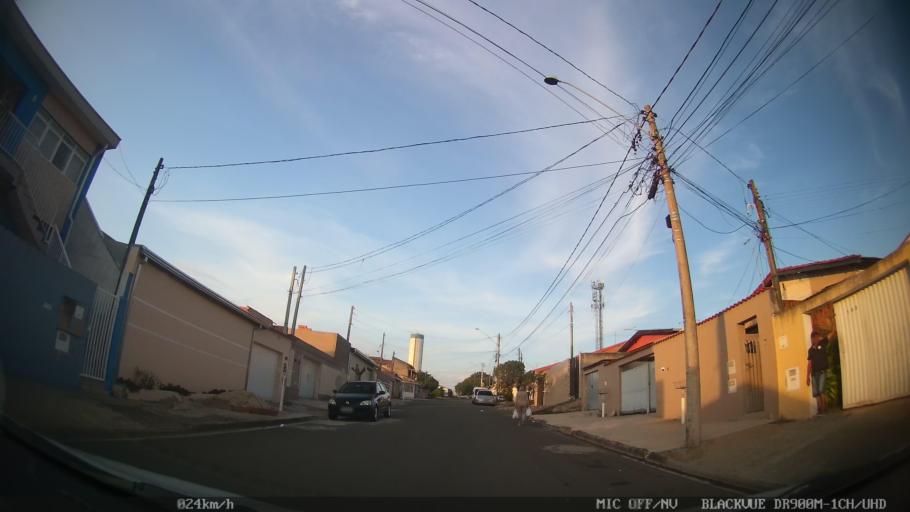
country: BR
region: Sao Paulo
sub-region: Campinas
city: Campinas
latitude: -22.9795
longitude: -47.1342
